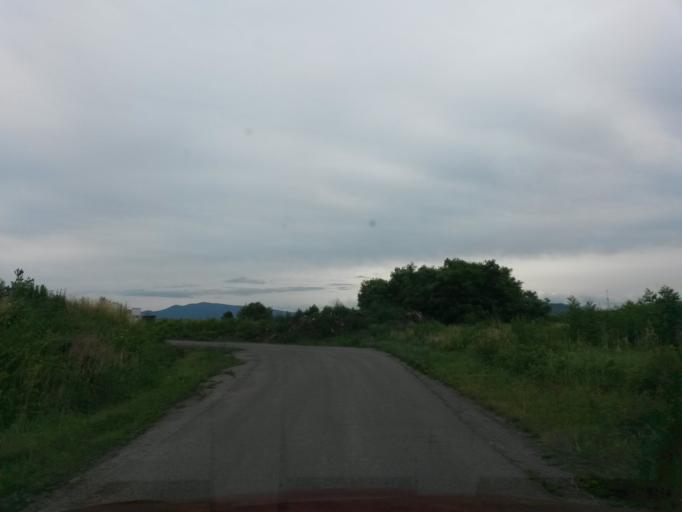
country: SK
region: Banskobystricky
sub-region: Okres Banska Bystrica
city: Zvolen
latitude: 48.5607
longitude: 19.2410
